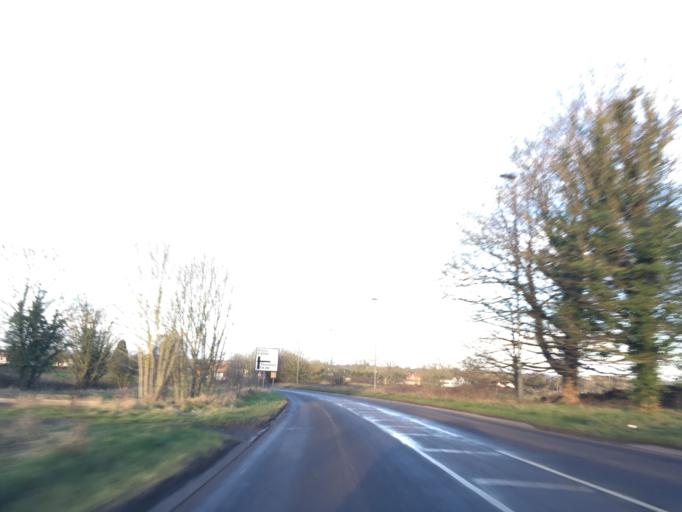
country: GB
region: England
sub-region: South Gloucestershire
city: Tytherington
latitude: 51.5520
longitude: -2.4619
